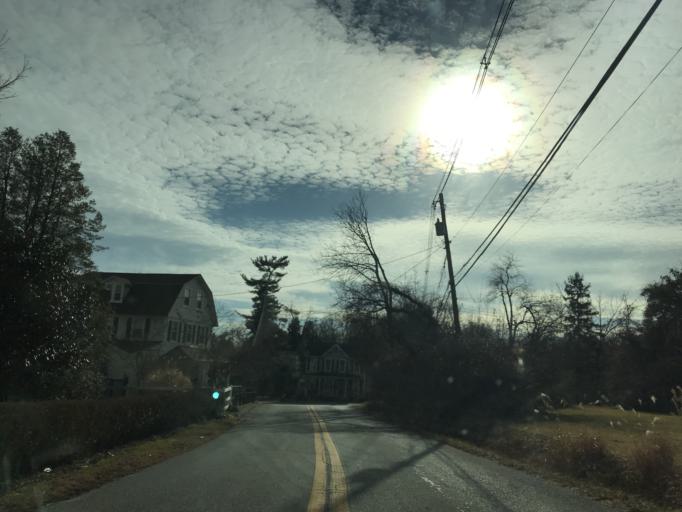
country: US
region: Maryland
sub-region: Baltimore County
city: Kingsville
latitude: 39.4380
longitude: -76.4020
